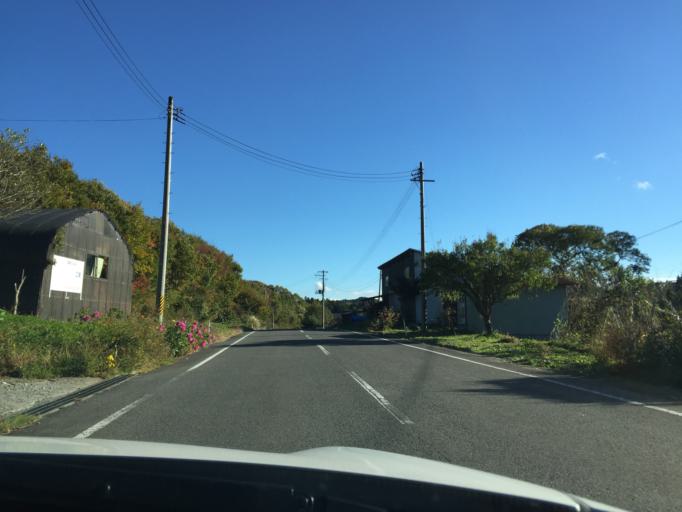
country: JP
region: Fukushima
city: Ishikawa
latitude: 37.2499
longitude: 140.5550
